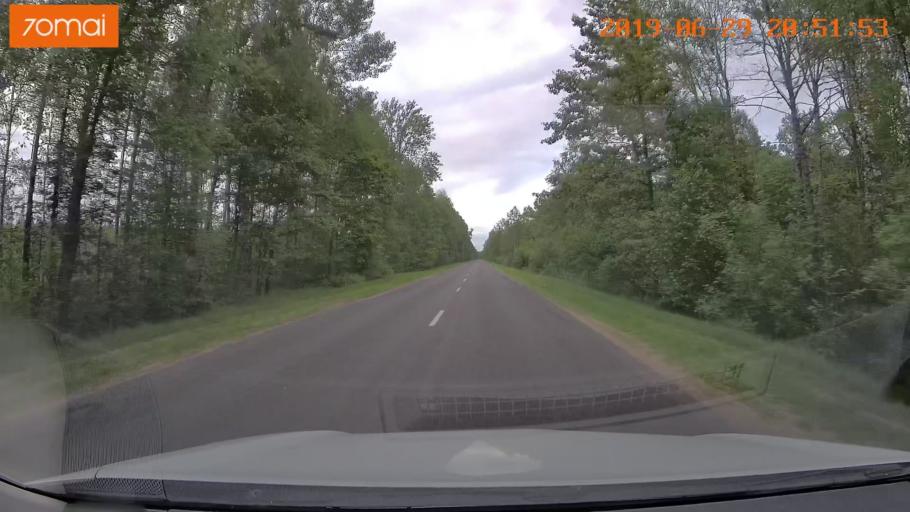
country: BY
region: Brest
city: Hantsavichy
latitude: 52.6932
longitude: 26.3555
